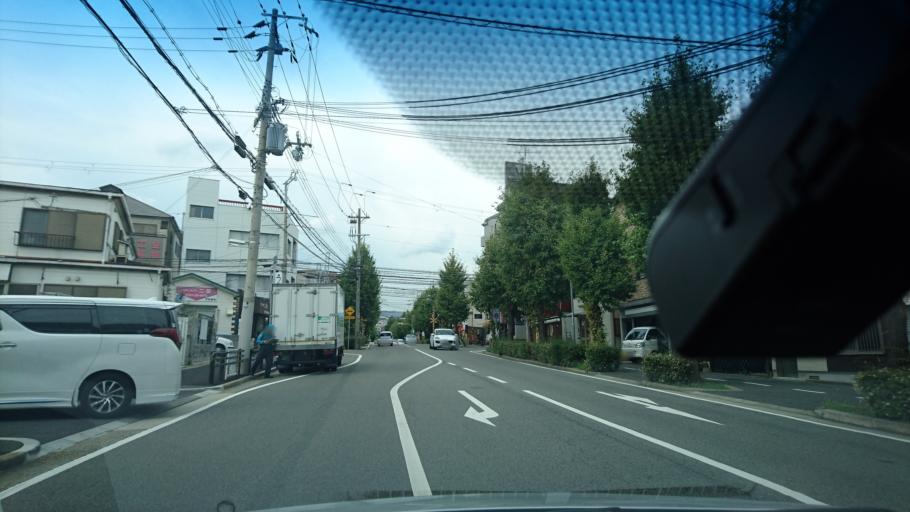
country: JP
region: Hyogo
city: Ashiya
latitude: 34.7314
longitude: 135.3170
